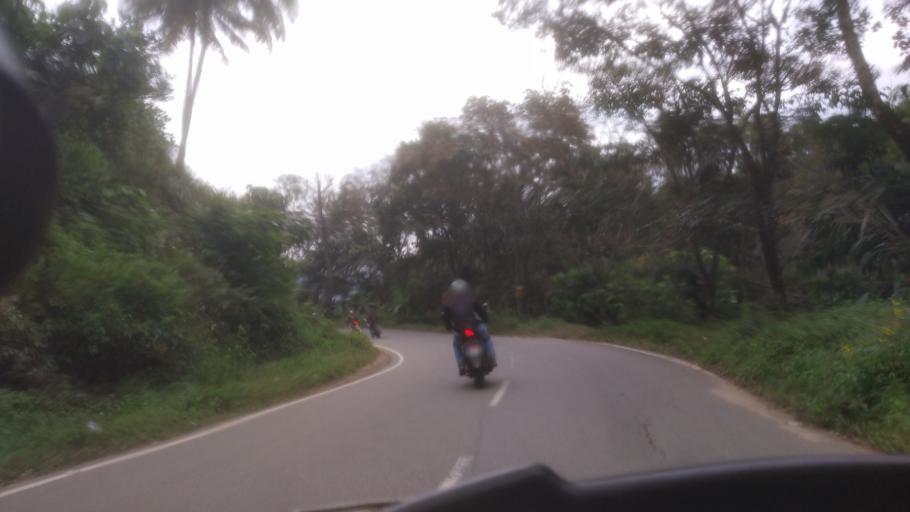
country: IN
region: Kerala
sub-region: Idukki
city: Munnar
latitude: 9.9834
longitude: 76.9903
